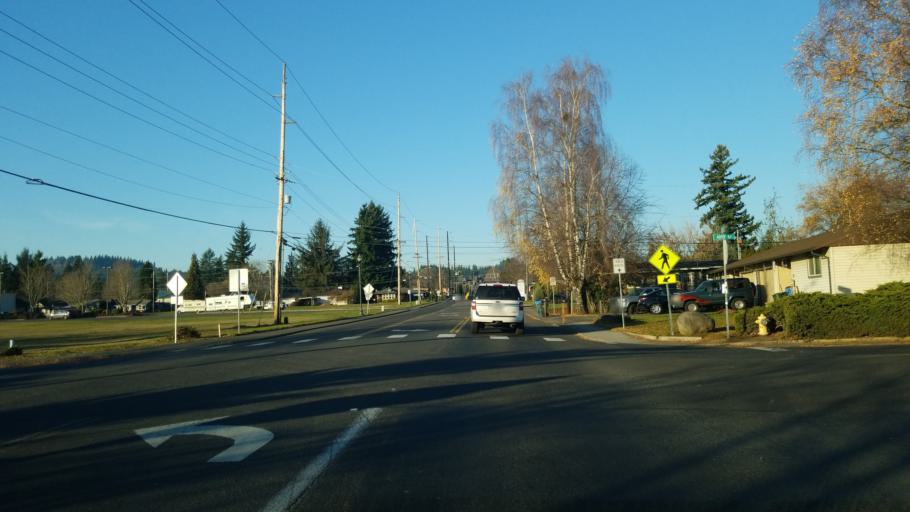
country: US
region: Washington
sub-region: Clark County
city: Washougal
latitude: 45.5759
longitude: -122.3369
